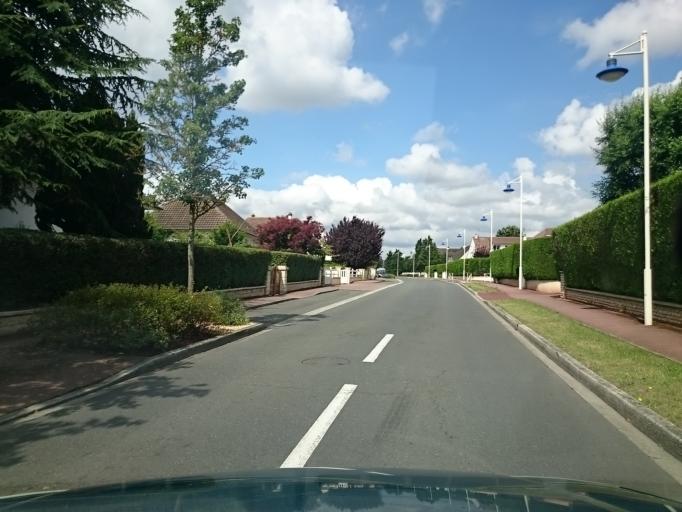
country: FR
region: Lower Normandy
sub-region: Departement du Calvados
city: Ifs
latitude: 49.1445
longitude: -0.3474
